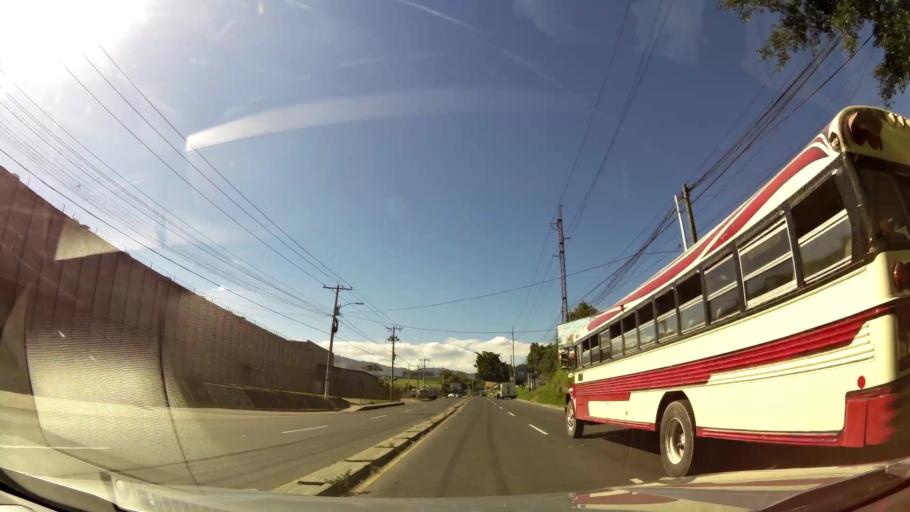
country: GT
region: Guatemala
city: Villa Nueva
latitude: 14.5324
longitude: -90.5975
